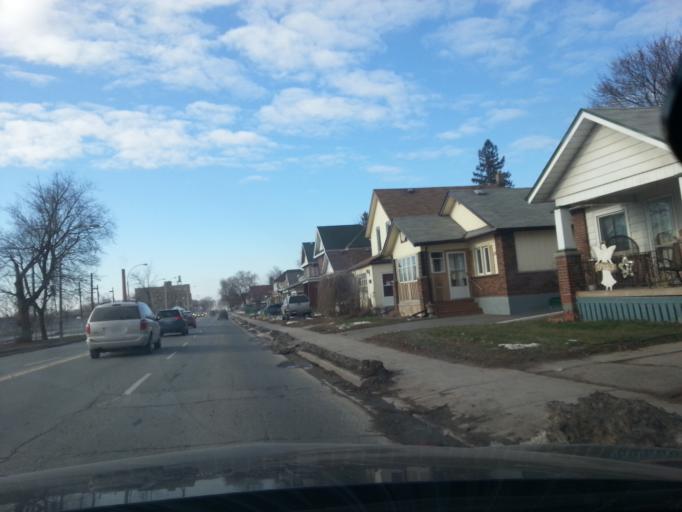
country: CA
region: Ontario
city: Peterborough
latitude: 44.2888
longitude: -78.3181
